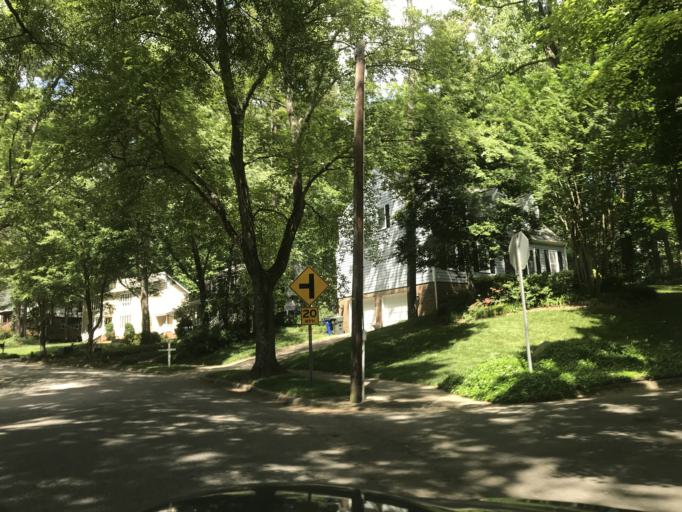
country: US
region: North Carolina
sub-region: Wake County
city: West Raleigh
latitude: 35.8569
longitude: -78.6255
